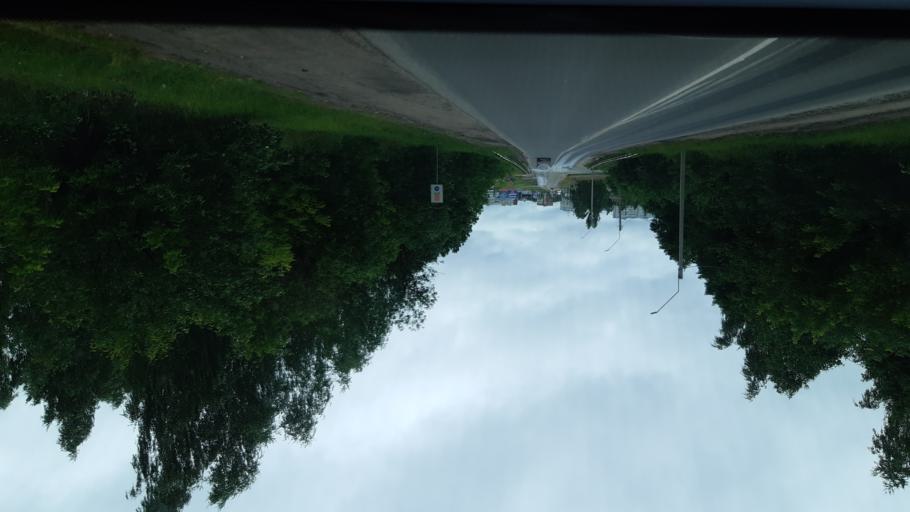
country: RU
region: Smolensk
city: Desnogorsk
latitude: 54.1380
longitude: 33.2779
